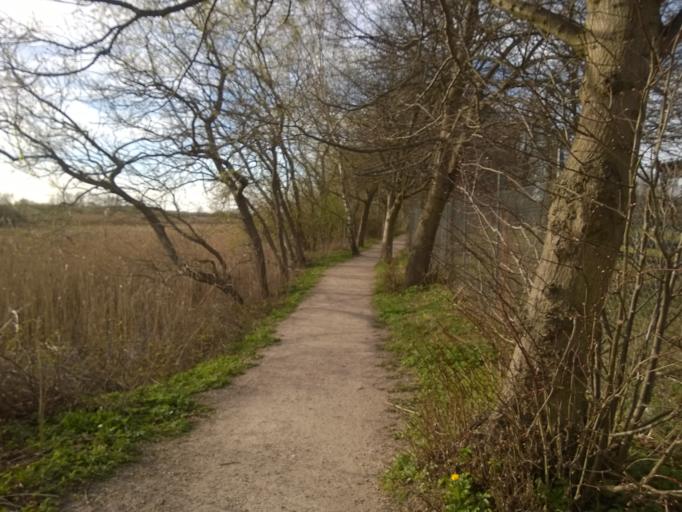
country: SE
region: Skane
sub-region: Kristianstads Kommun
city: Kristianstad
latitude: 56.0340
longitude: 14.1466
